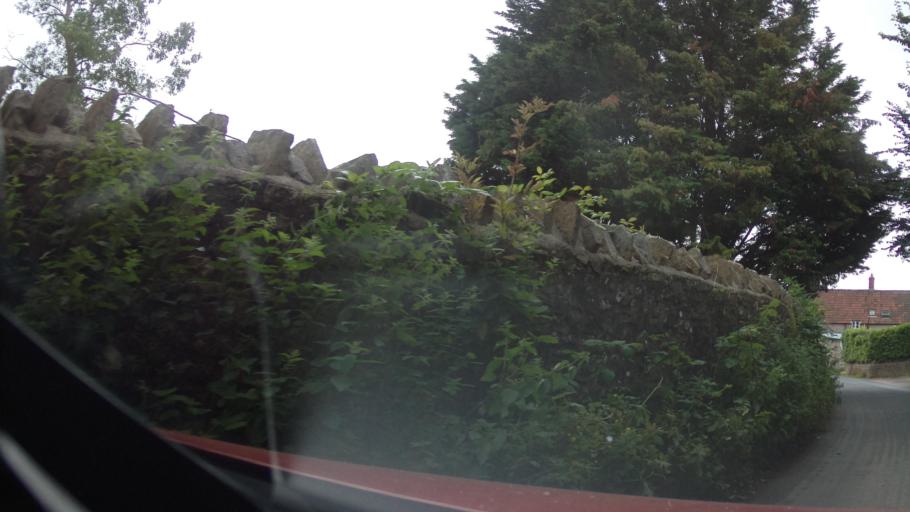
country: GB
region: England
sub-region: Somerset
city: Evercreech
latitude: 51.1526
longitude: -2.4958
